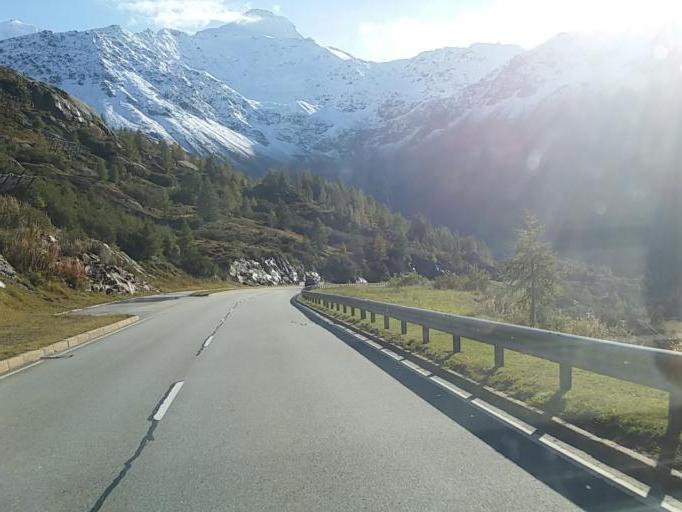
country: CH
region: Valais
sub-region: Brig District
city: Brig
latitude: 46.2362
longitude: 8.0195
